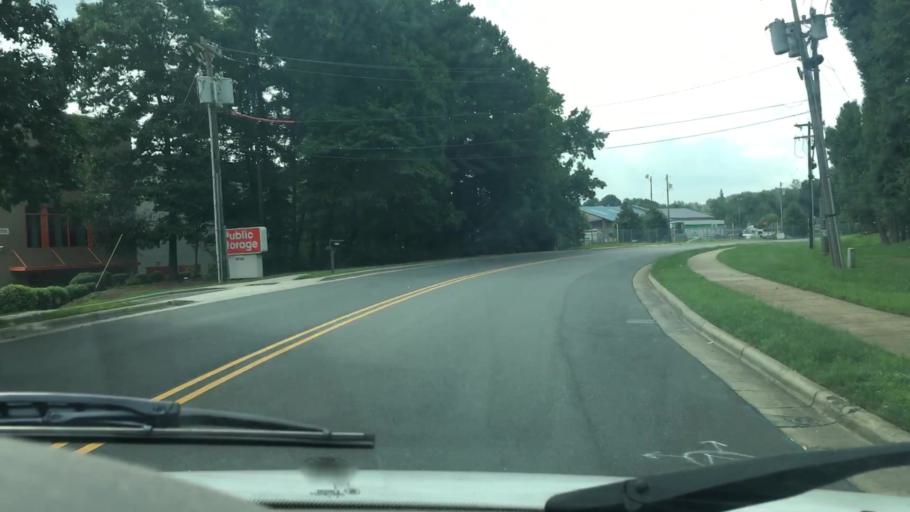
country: US
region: North Carolina
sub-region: Mecklenburg County
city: Charlotte
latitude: 35.3116
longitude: -80.8493
